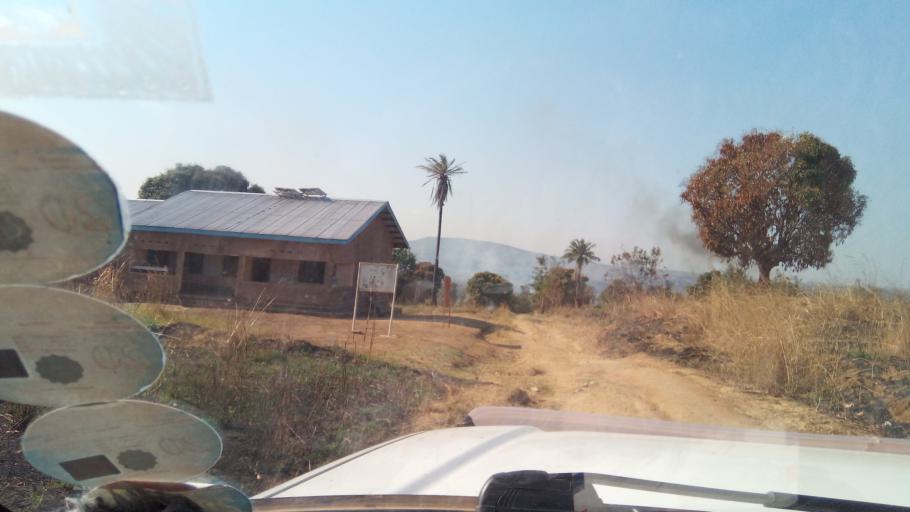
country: CD
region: Katanga
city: Kalemie
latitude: -5.9029
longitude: 29.1263
